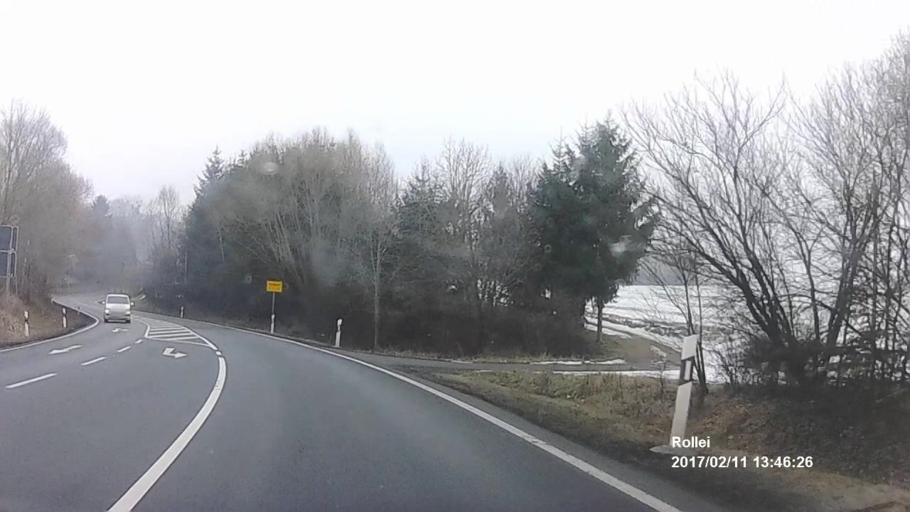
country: DE
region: Thuringia
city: Etzelsrode
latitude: 51.5414
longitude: 10.5983
